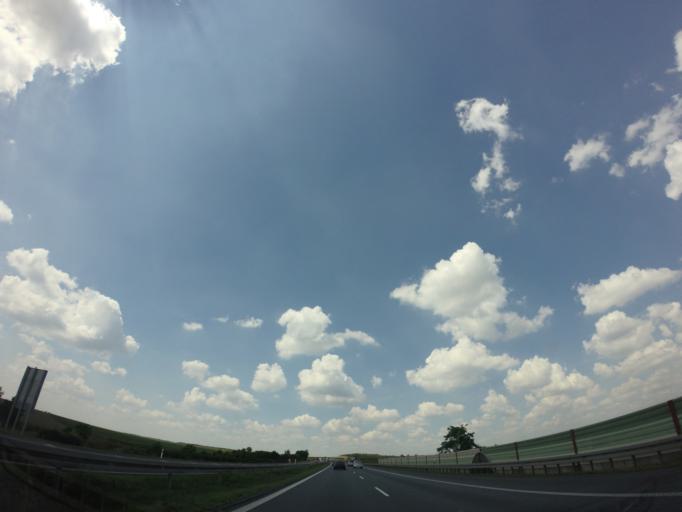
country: PL
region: Opole Voivodeship
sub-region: Powiat opolski
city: Proszkow
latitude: 50.5747
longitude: 17.8495
